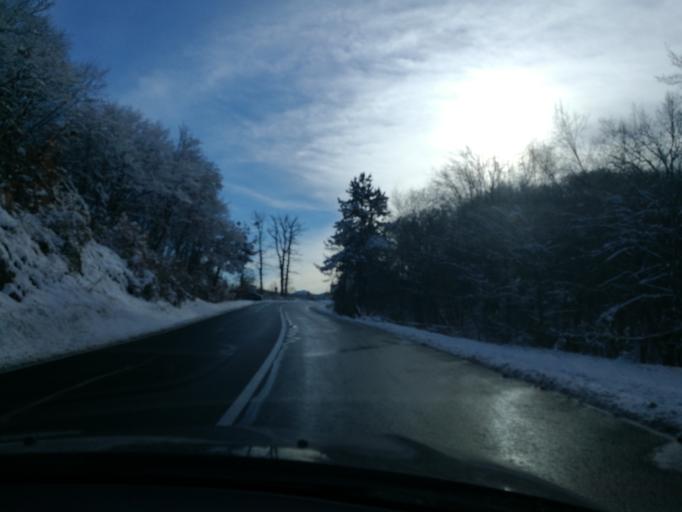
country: RO
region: Brasov
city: Brasov
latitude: 45.6400
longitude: 25.5620
